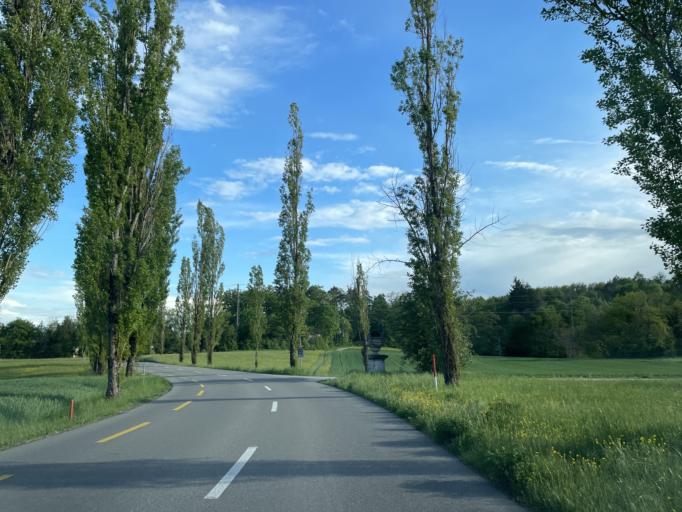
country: CH
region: Schaffhausen
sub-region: Bezirk Reiat
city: Stetten
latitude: 47.7319
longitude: 8.6603
